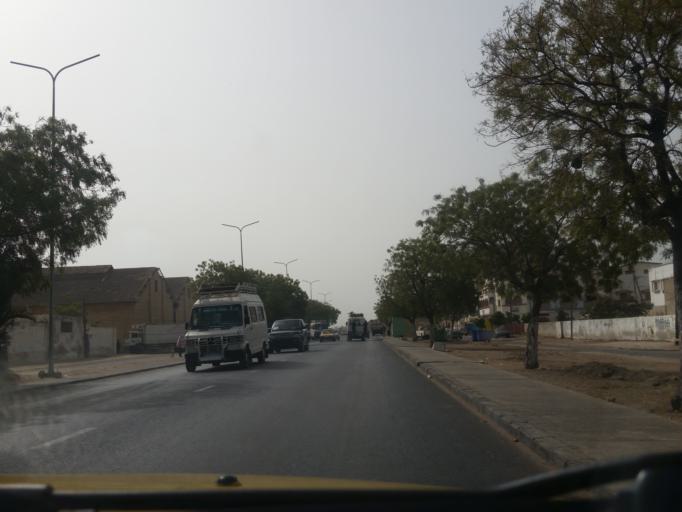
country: SN
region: Dakar
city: Pikine
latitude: 14.7128
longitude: -17.2684
